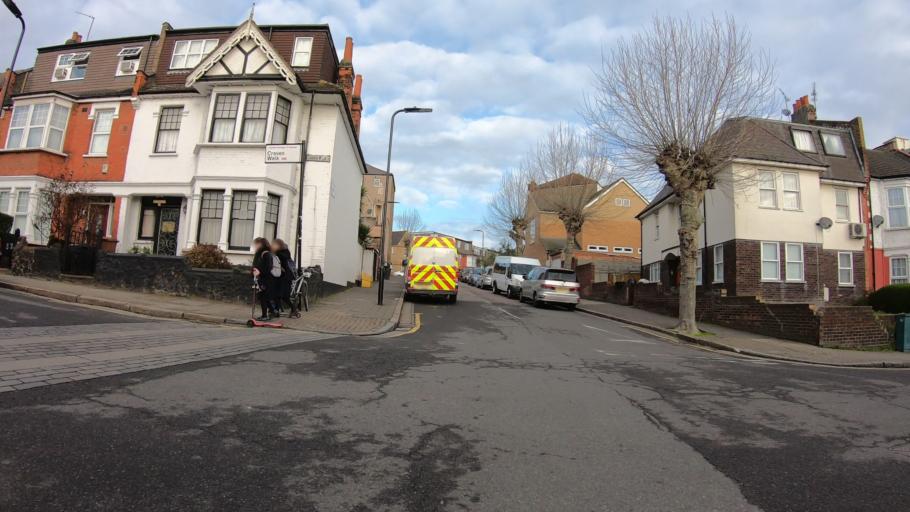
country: GB
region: England
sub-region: Greater London
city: Hackney
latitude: 51.5695
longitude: -0.0535
